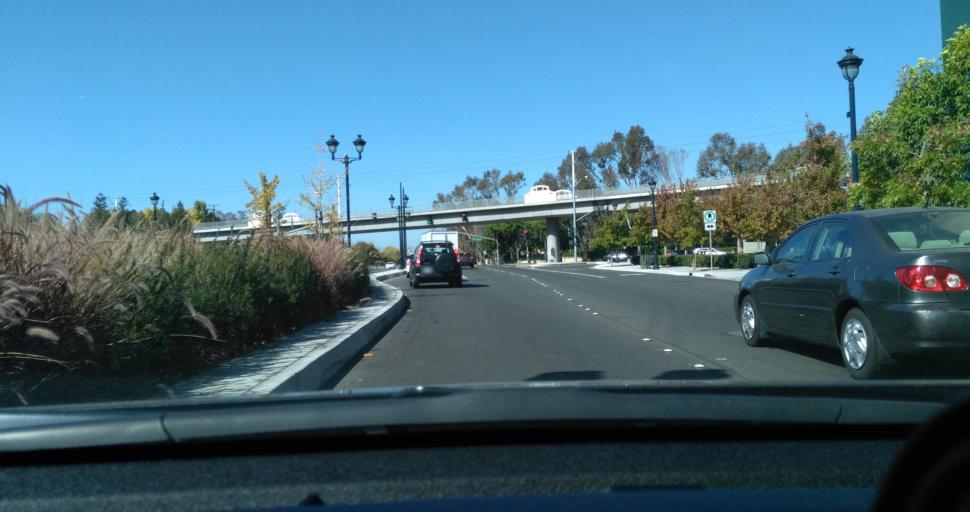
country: US
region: California
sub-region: Santa Clara County
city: Milpitas
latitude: 37.4144
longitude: -121.9046
